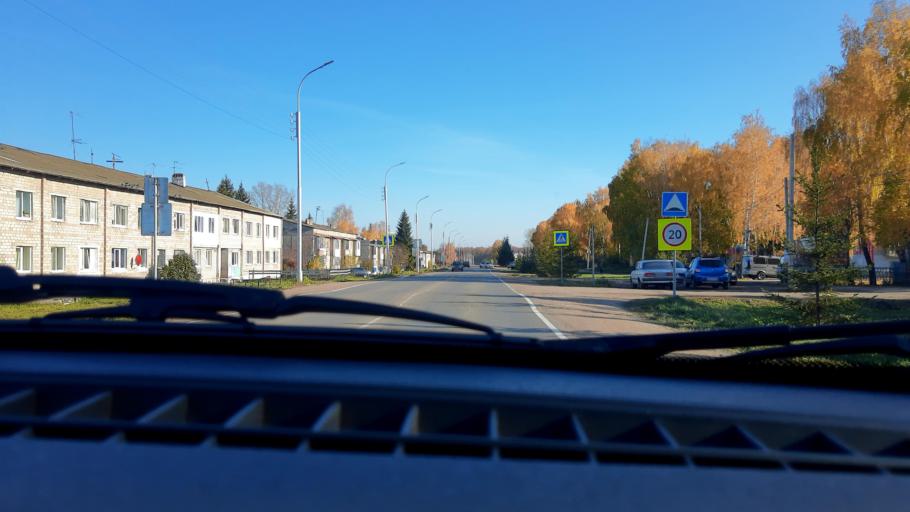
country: RU
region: Bashkortostan
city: Mikhaylovka
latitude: 54.8135
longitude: 55.8032
